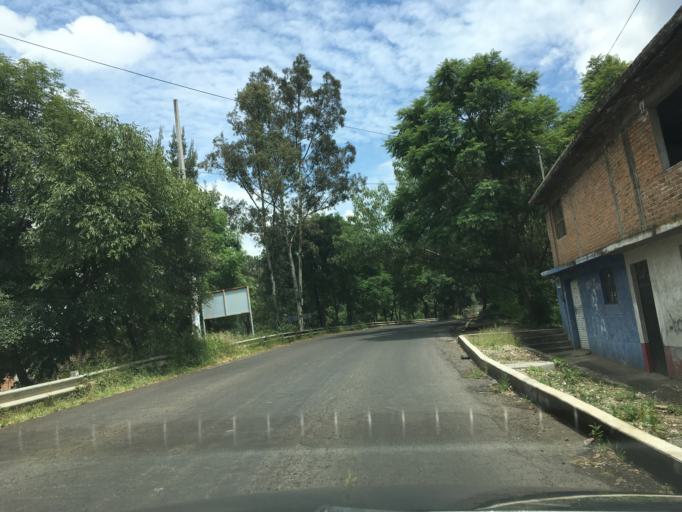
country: MX
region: Michoacan
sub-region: Morelia
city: Morelos
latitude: 19.6543
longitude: -101.2316
